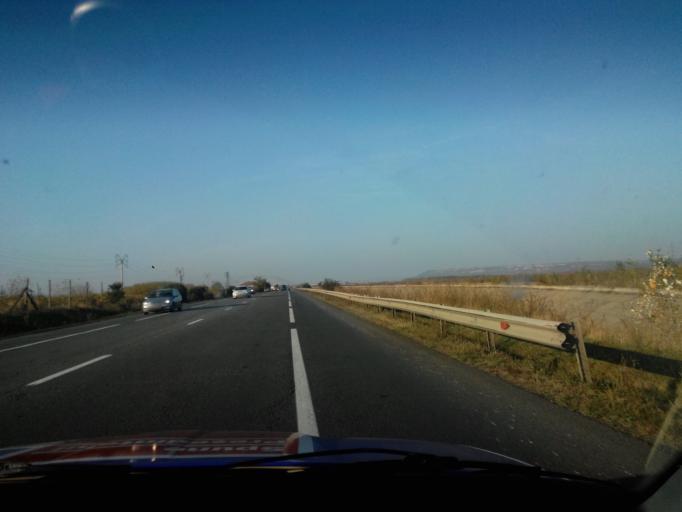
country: RO
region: Vrancea
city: Marasheshty
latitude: 45.8899
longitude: 27.2100
